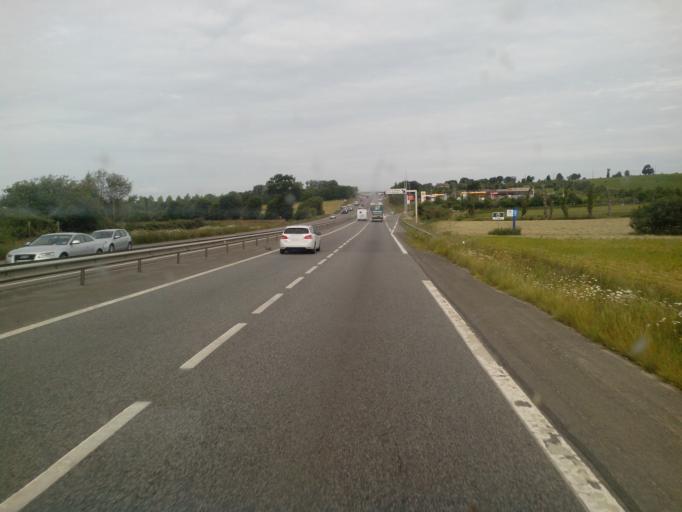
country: FR
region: Brittany
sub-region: Departement d'Ille-et-Vilaine
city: Saint-Gilles
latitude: 48.1639
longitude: -1.8622
